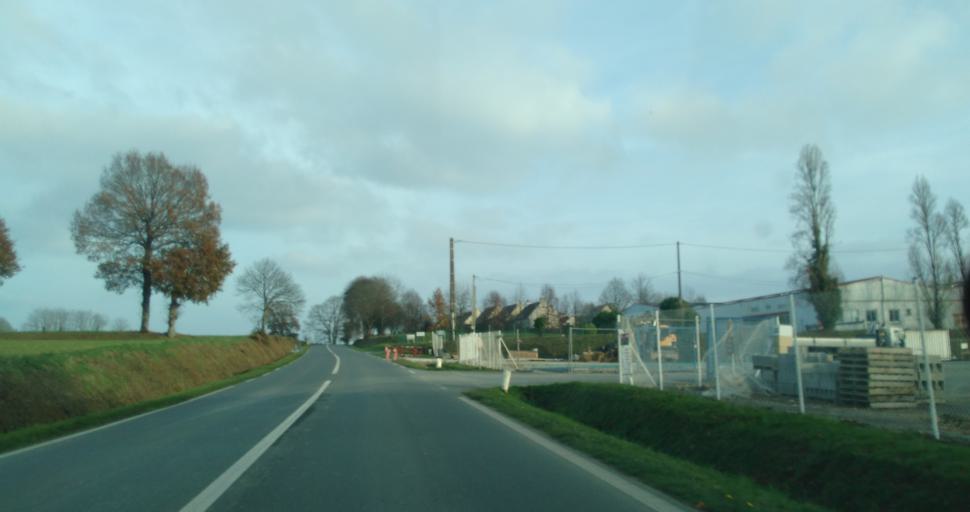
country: FR
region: Brittany
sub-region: Departement d'Ille-et-Vilaine
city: Vezin-le-Coquet
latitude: 48.1209
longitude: -1.7714
